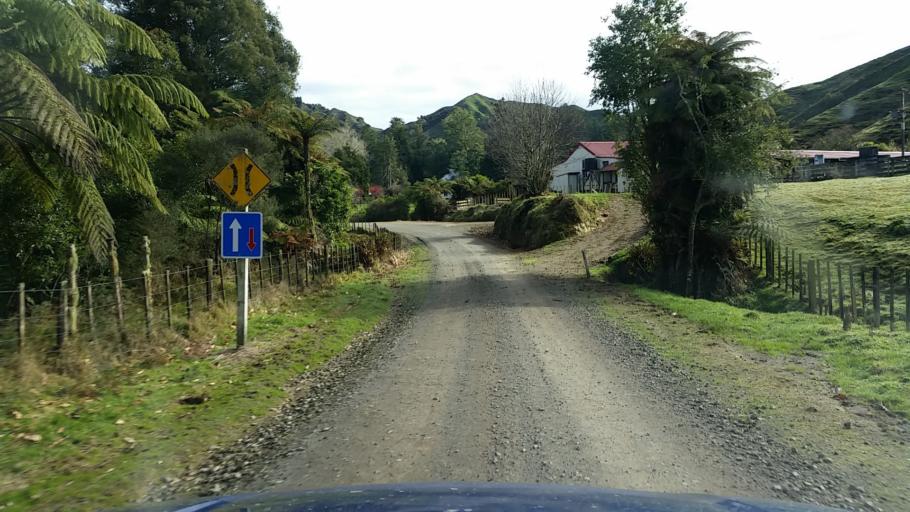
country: NZ
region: Taranaki
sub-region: New Plymouth District
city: Waitara
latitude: -39.1029
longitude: 174.8431
